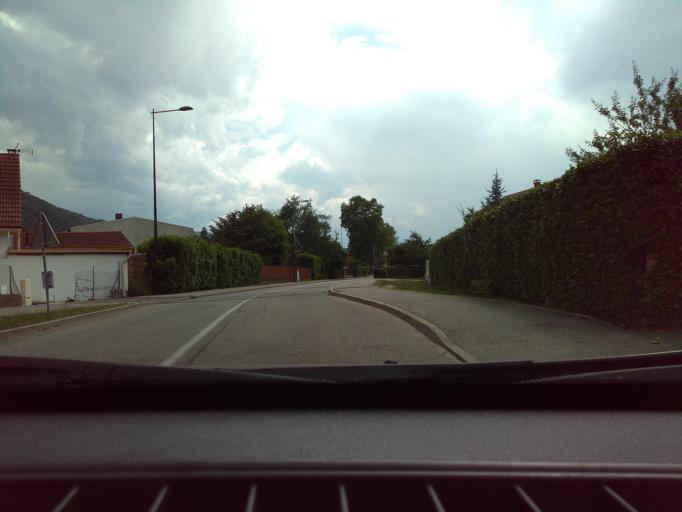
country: FR
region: Rhone-Alpes
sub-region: Departement de l'Isere
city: Saint-Martin-d'Heres
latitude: 45.1676
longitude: 5.7678
